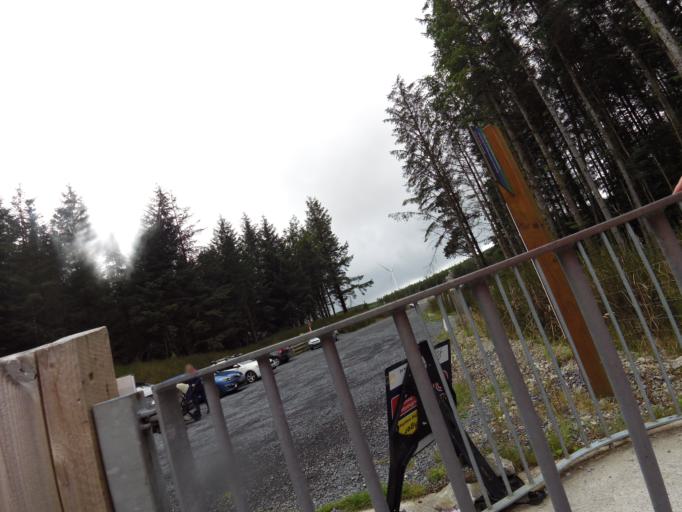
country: IE
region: Connaught
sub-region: County Galway
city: Oughterard
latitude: 53.3823
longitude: -9.3737
